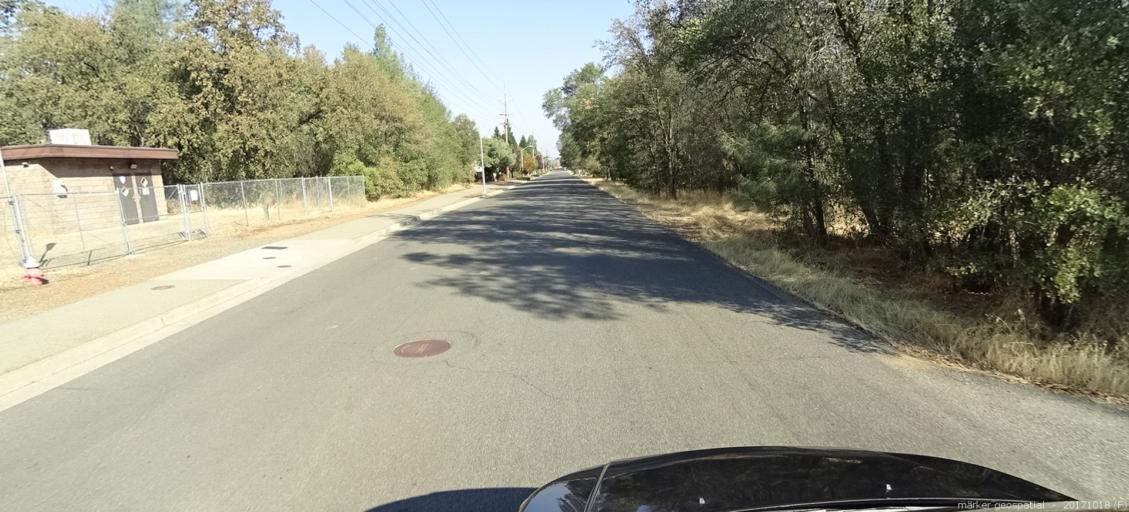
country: US
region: California
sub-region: Shasta County
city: Palo Cedro
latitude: 40.5405
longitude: -122.3146
